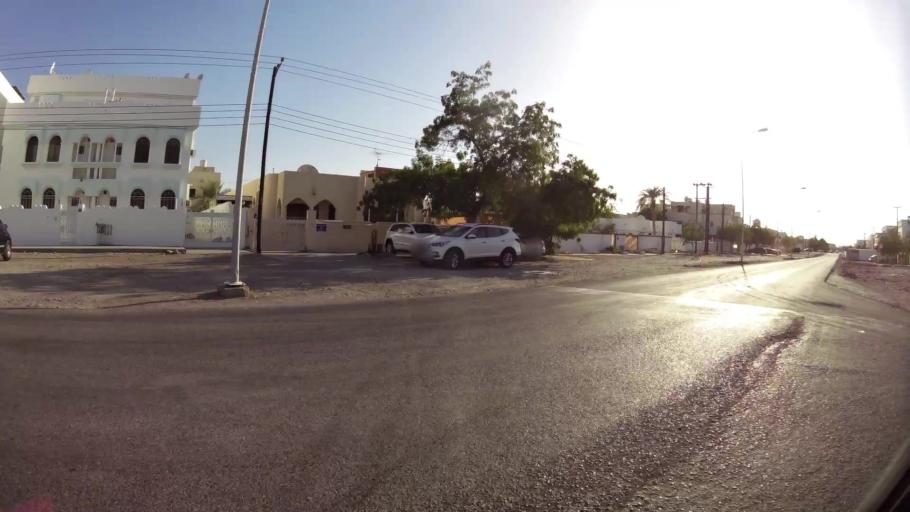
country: OM
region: Muhafazat Masqat
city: As Sib al Jadidah
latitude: 23.6347
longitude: 58.1992
